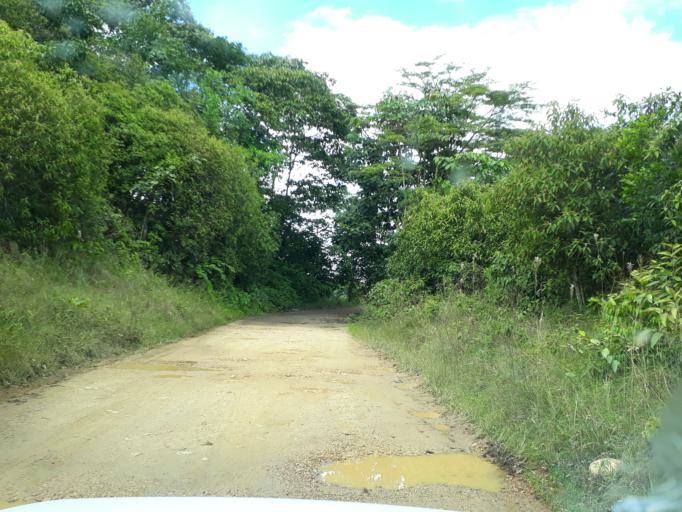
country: CO
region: Cundinamarca
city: Medina
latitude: 4.5884
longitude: -73.3135
